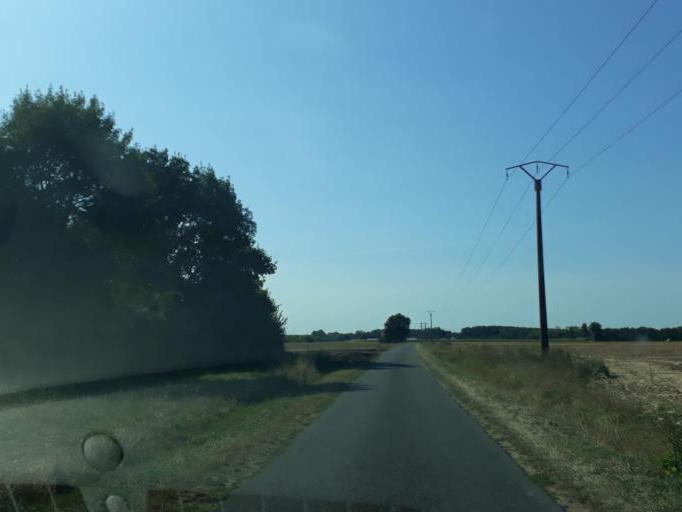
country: FR
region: Centre
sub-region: Departement du Loir-et-Cher
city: Selles-sur-Cher
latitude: 47.2676
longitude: 1.5901
